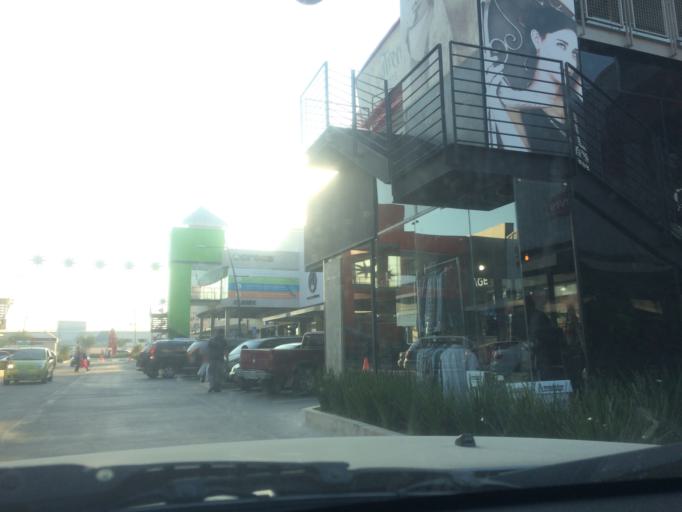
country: MX
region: Guanajuato
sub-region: Leon
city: Fraccionamiento Paraiso Real
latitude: 21.0868
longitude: -101.6143
